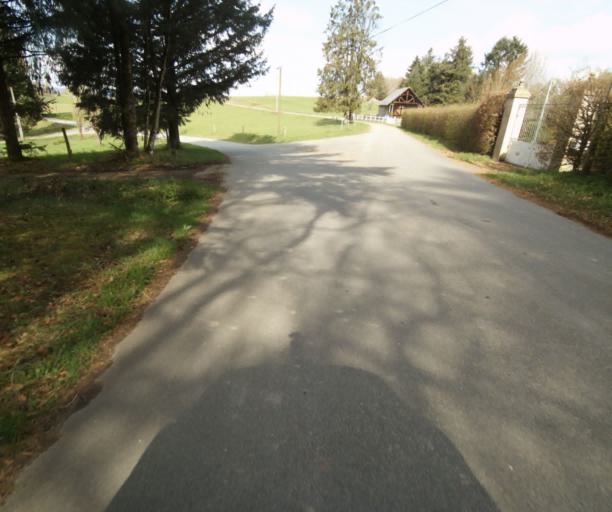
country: FR
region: Limousin
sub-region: Departement de la Correze
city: Correze
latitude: 45.3510
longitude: 1.8719
